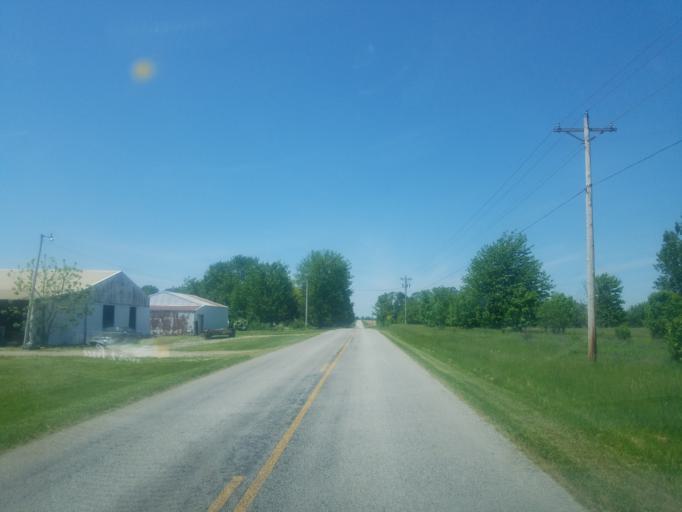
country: US
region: Ohio
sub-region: Huron County
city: New London
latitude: 41.1160
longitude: -82.3755
